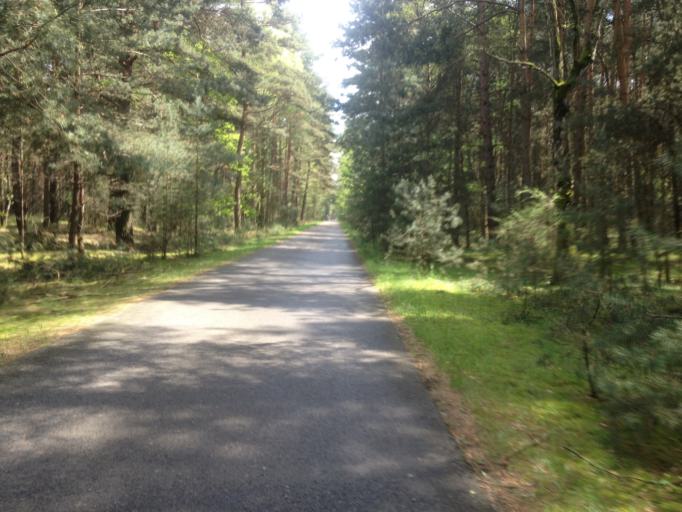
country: DE
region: Brandenburg
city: Briesen
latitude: 51.8082
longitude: 14.2595
